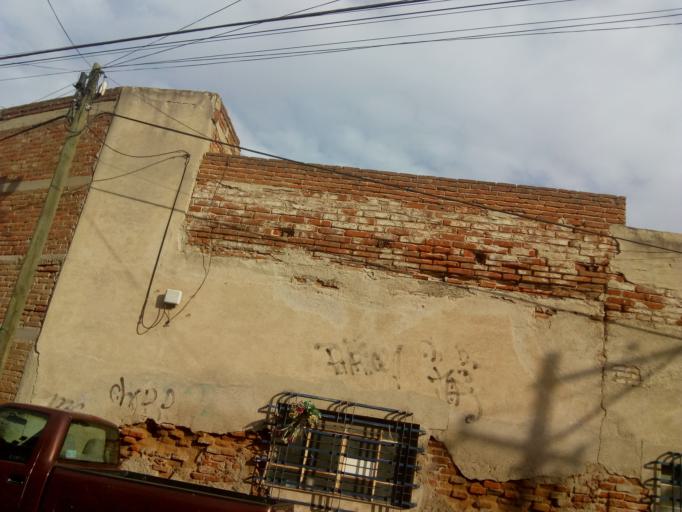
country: MX
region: Guanajuato
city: Leon
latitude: 21.1371
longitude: -101.6811
